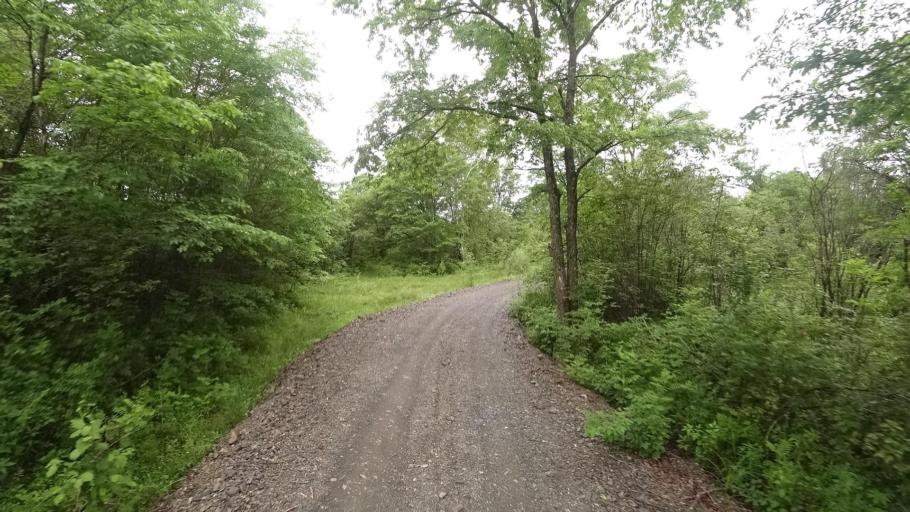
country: RU
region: Khabarovsk Krai
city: Amursk
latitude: 49.9046
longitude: 136.1340
